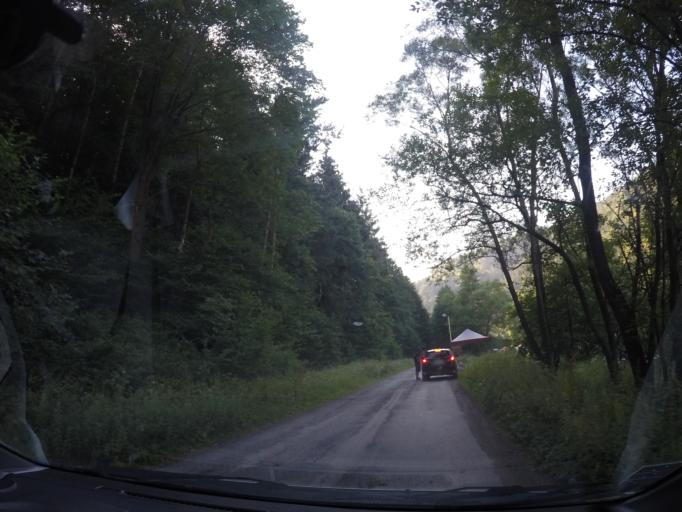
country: SK
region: Nitriansky
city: Bojnice
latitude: 48.9069
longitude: 18.6030
